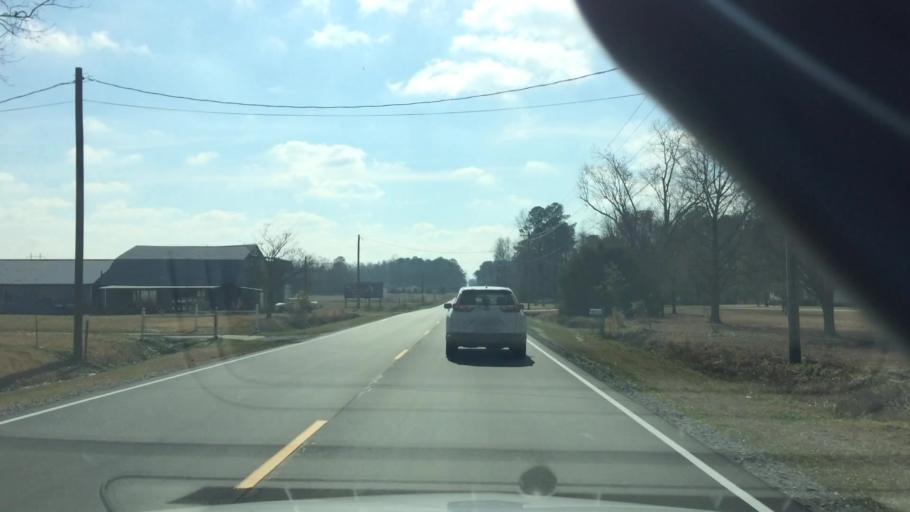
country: US
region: North Carolina
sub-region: Duplin County
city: Beulaville
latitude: 34.9703
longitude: -77.7624
